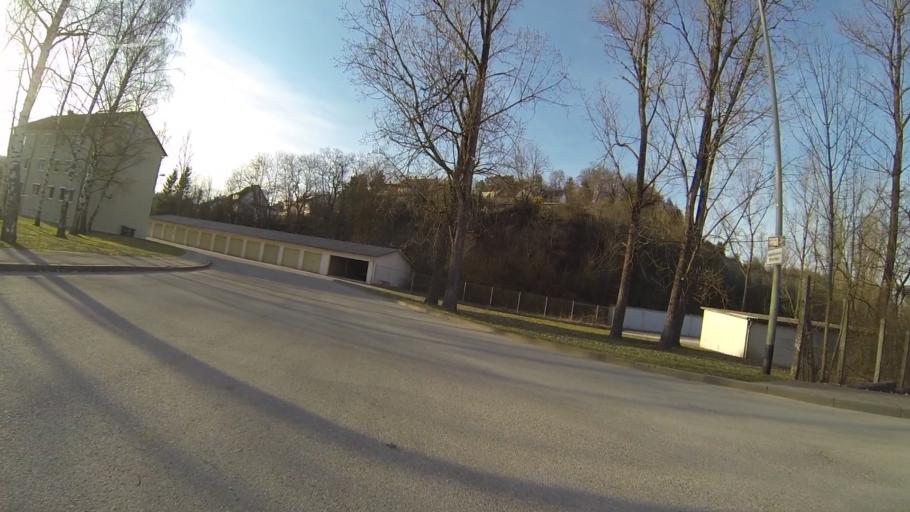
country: DE
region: Baden-Wuerttemberg
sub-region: Regierungsbezirk Stuttgart
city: Heidenheim an der Brenz
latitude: 48.6559
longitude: 10.1648
